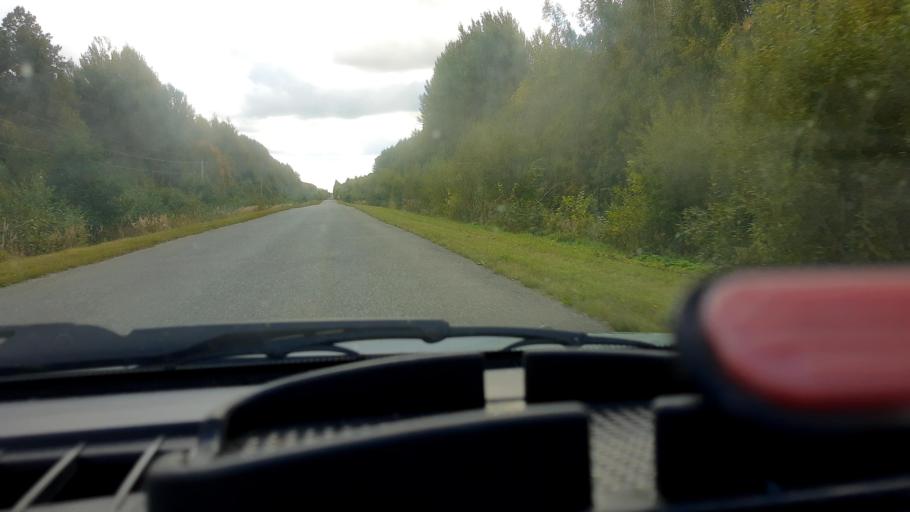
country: RU
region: Mariy-El
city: Kilemary
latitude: 56.9139
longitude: 46.7251
